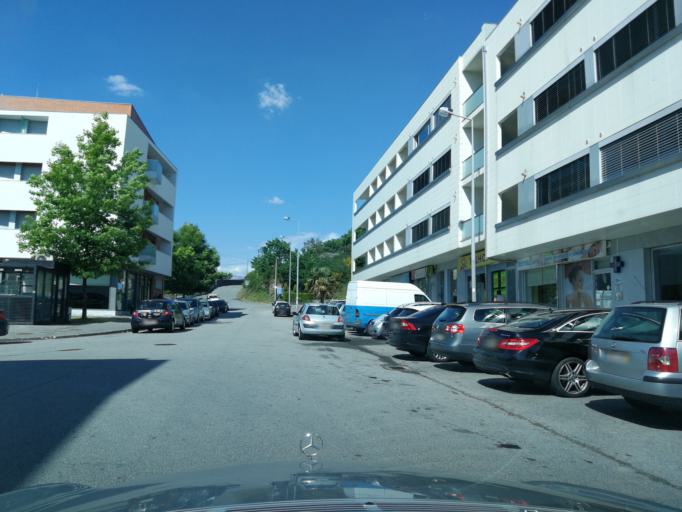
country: PT
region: Braga
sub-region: Braga
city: Adaufe
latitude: 41.5623
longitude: -8.3835
